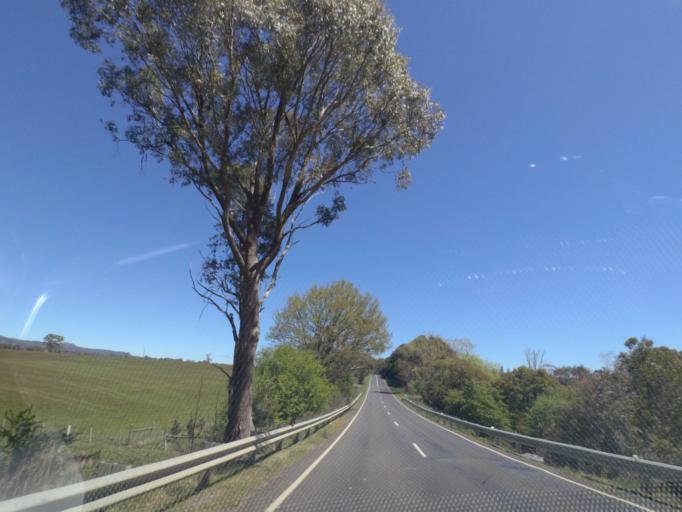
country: AU
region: Victoria
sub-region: Hume
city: Sunbury
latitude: -37.3140
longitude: 144.6696
